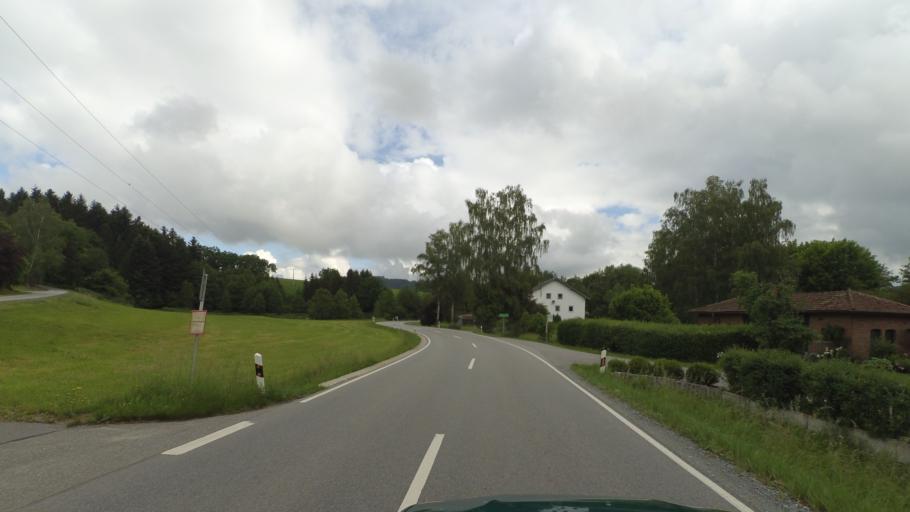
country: DE
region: Bavaria
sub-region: Lower Bavaria
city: Konzell
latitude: 49.0521
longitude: 12.7143
